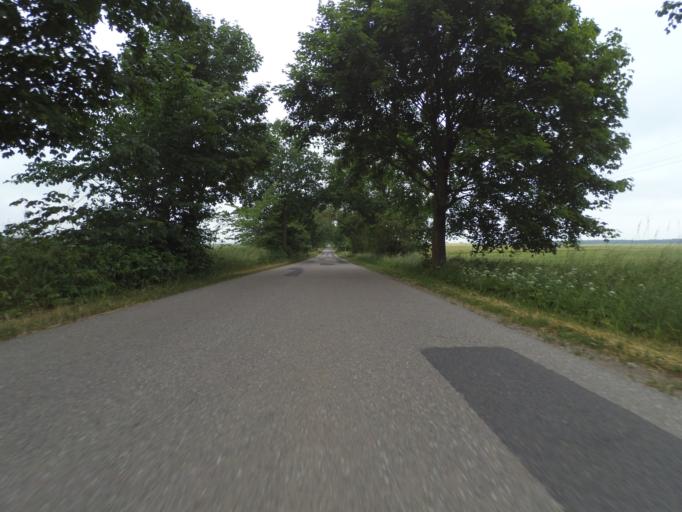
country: DE
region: Mecklenburg-Vorpommern
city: Lubz
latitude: 53.5097
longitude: 12.0475
